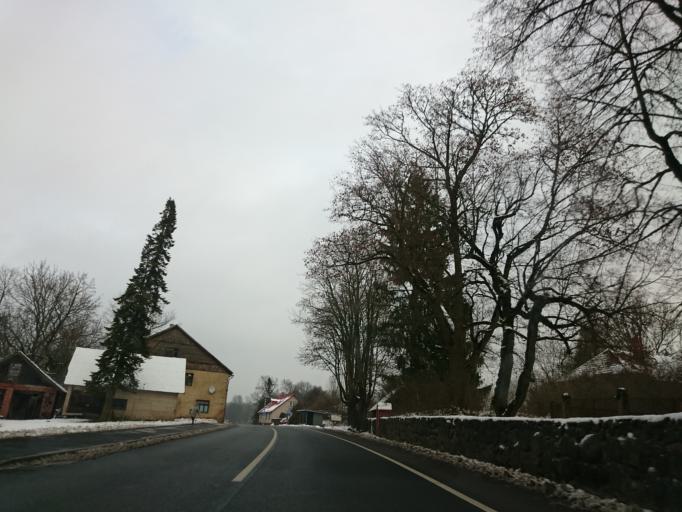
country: LV
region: Pargaujas
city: Stalbe
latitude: 57.3482
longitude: 24.9473
